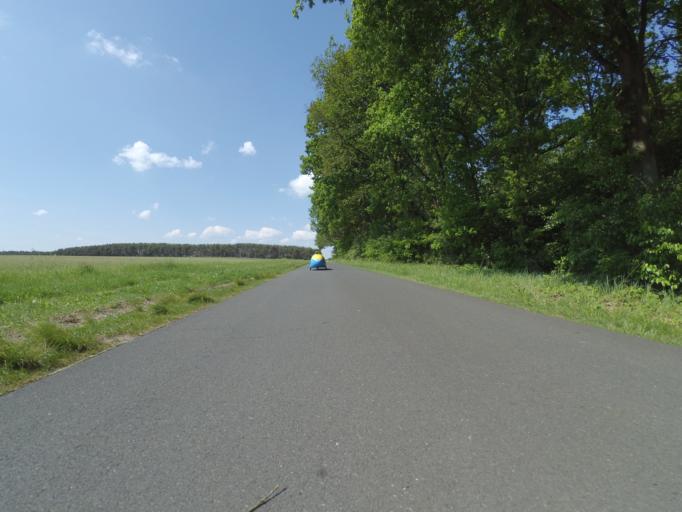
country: DE
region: Lower Saxony
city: Burgdorf
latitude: 52.5160
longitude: 9.9450
